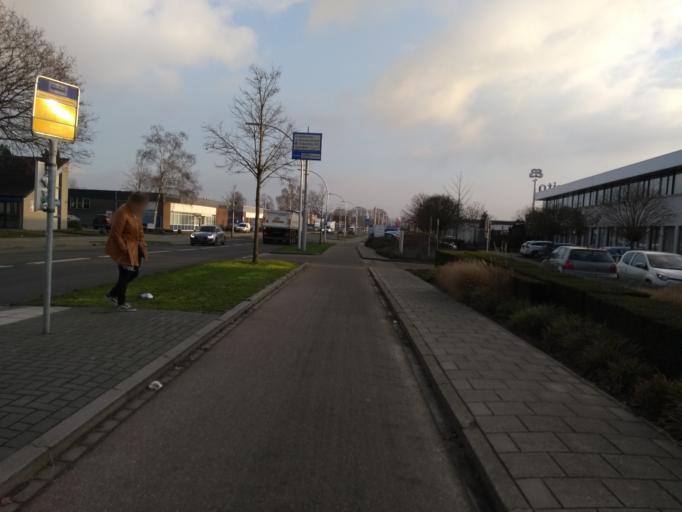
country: NL
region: Overijssel
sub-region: Gemeente Almelo
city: Almelo
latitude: 52.3728
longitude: 6.6394
